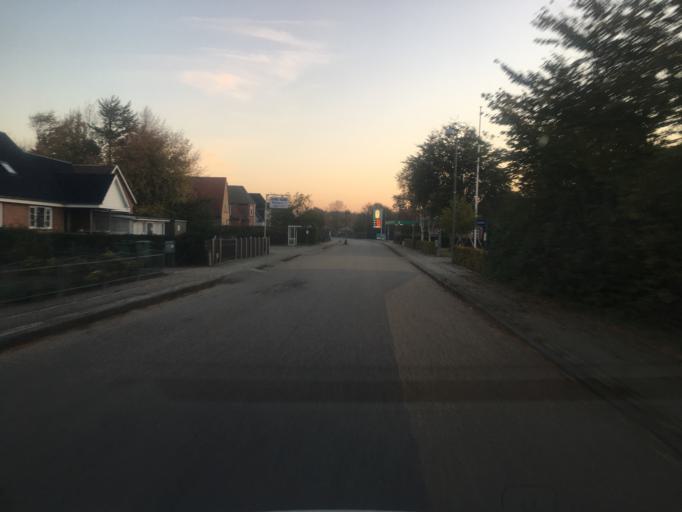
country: DE
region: Schleswig-Holstein
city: Bramstedtlund
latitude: 54.9388
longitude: 9.0823
